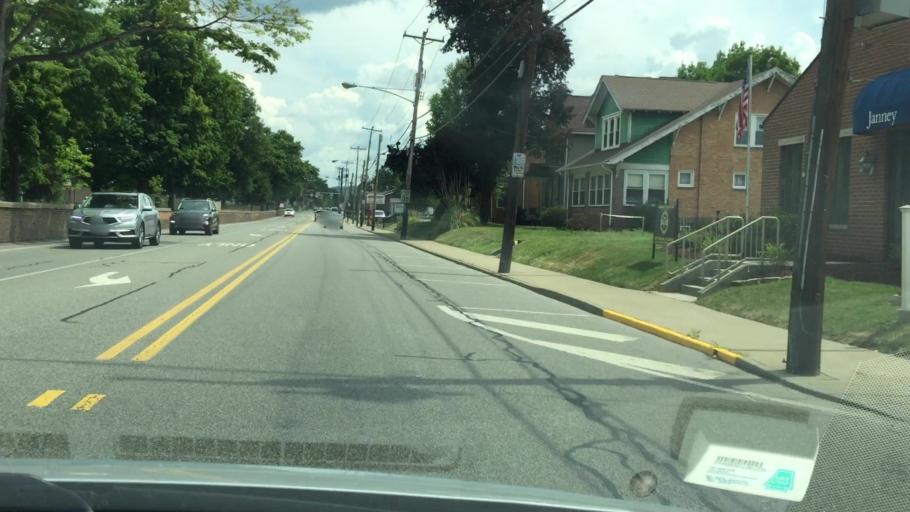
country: US
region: Pennsylvania
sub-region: Beaver County
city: Beaver
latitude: 40.6907
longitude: -80.3156
